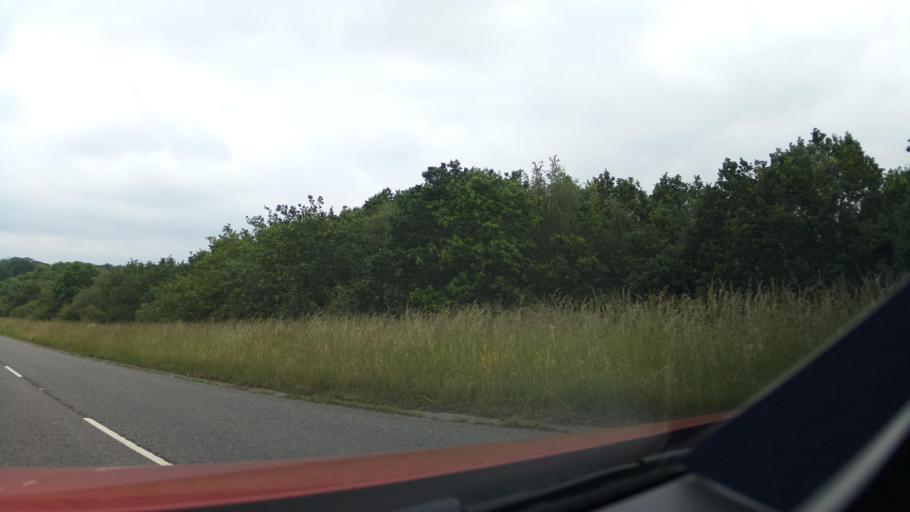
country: GB
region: England
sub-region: District of Rutland
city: Burley
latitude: 52.6747
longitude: -0.6706
